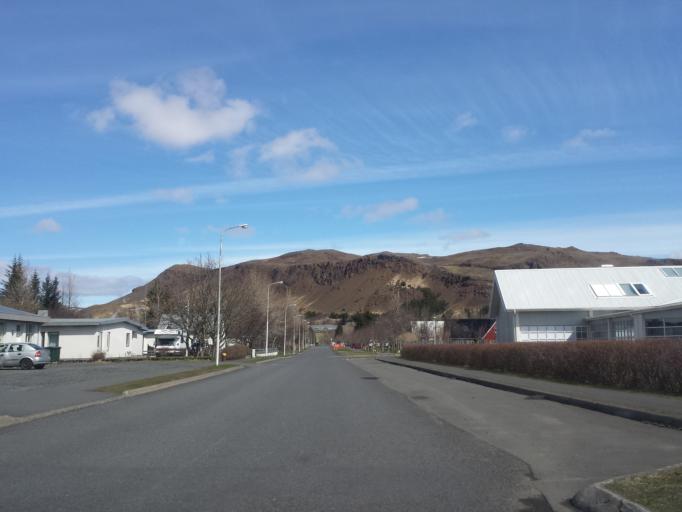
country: IS
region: South
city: Hveragerdi
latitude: 63.9963
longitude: -21.1858
